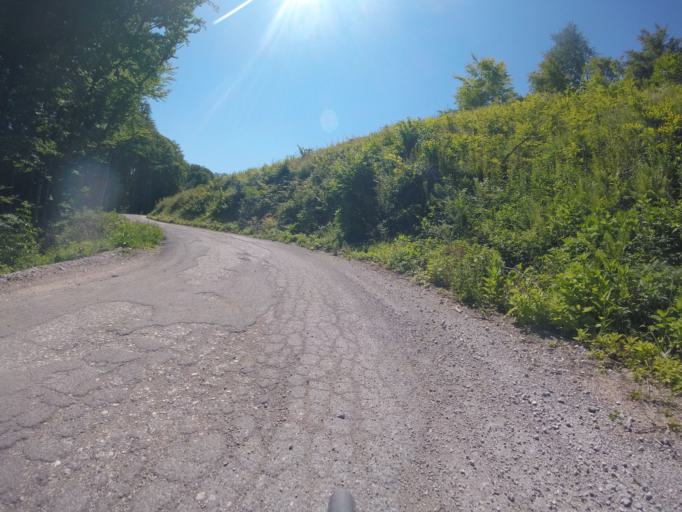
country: SI
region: Kostanjevica na Krki
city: Kostanjevica na Krki
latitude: 45.8145
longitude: 15.5135
